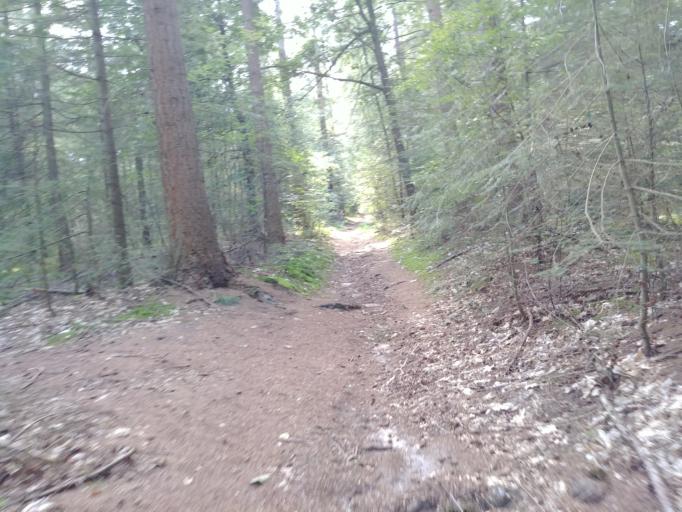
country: NL
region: Utrecht
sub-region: Gemeente Utrechtse Heuvelrug
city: Maarn
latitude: 52.0530
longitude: 5.3626
